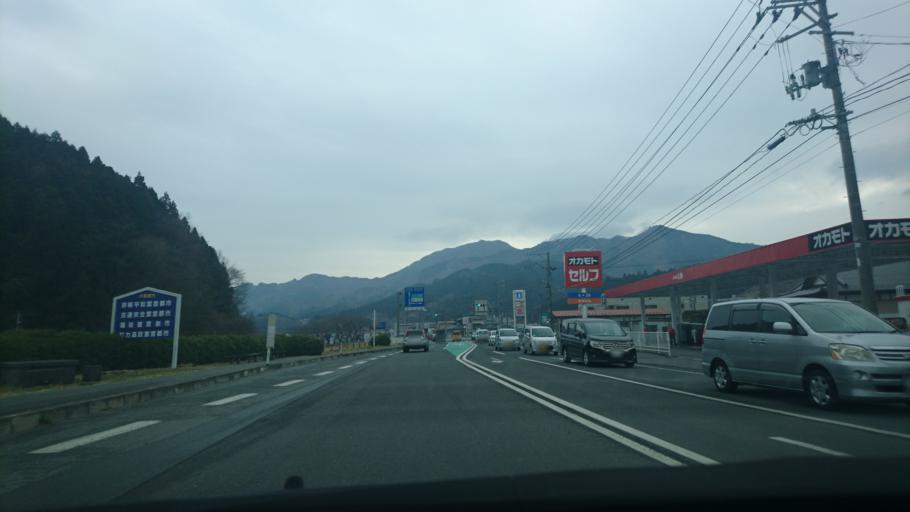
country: JP
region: Iwate
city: Ofunato
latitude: 39.0999
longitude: 141.7085
